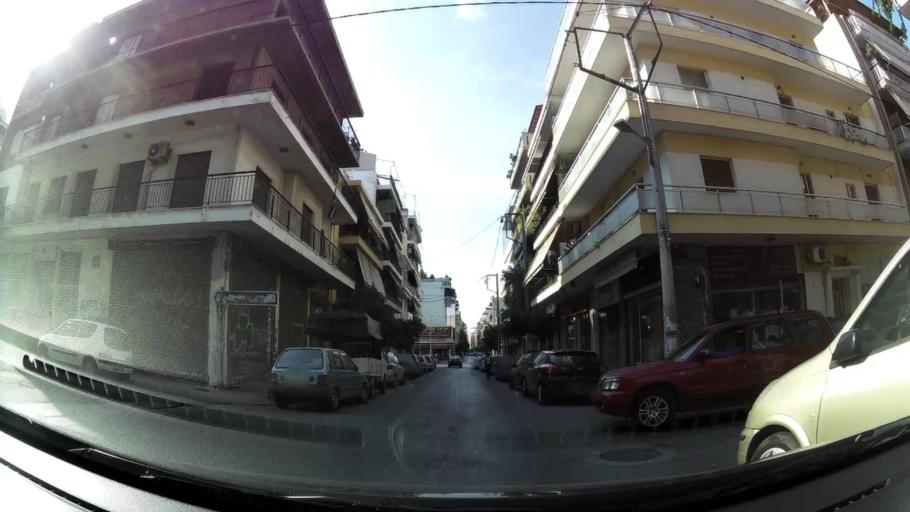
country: GR
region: Attica
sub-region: Nomarchia Athinas
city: Tavros
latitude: 37.9657
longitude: 23.7059
